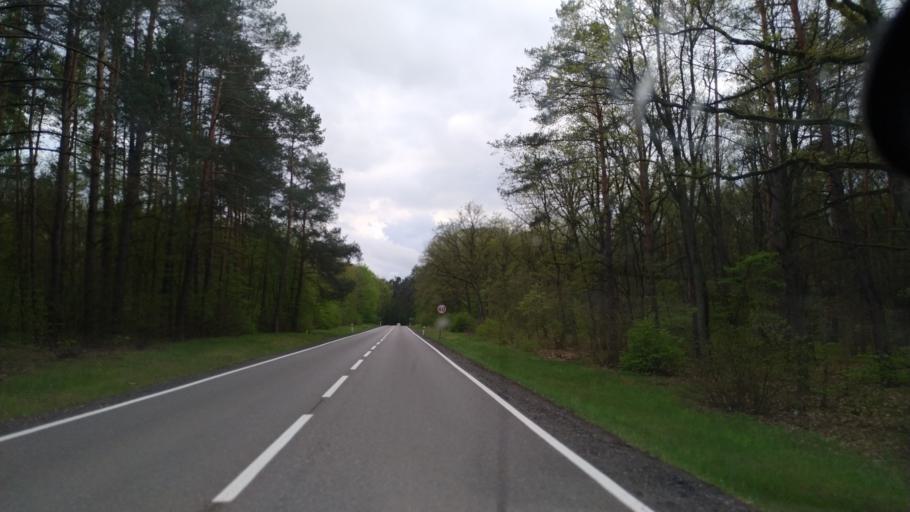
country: PL
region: Pomeranian Voivodeship
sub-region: Powiat kwidzynski
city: Ryjewo
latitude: 53.8099
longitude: 18.9683
